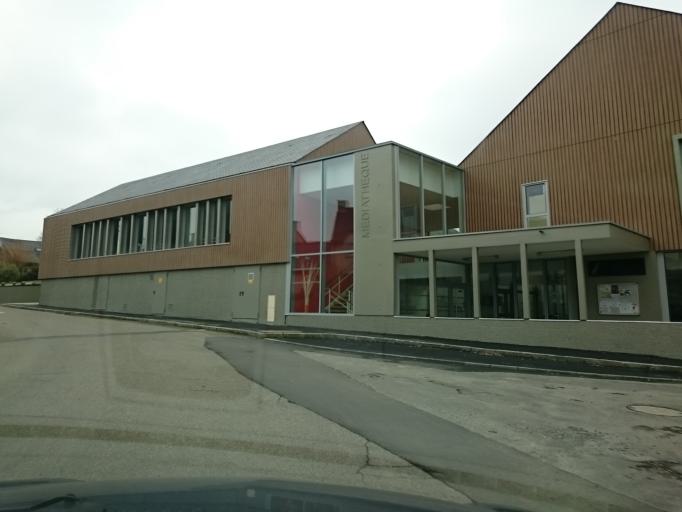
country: FR
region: Brittany
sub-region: Departement d'Ille-et-Vilaine
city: Chanteloup
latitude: 47.9662
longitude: -1.6141
